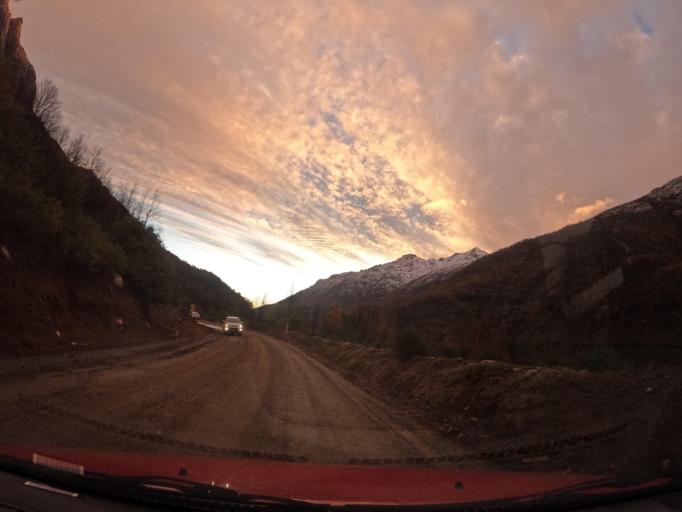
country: CL
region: Maule
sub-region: Provincia de Linares
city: Colbun
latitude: -35.8564
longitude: -71.1709
